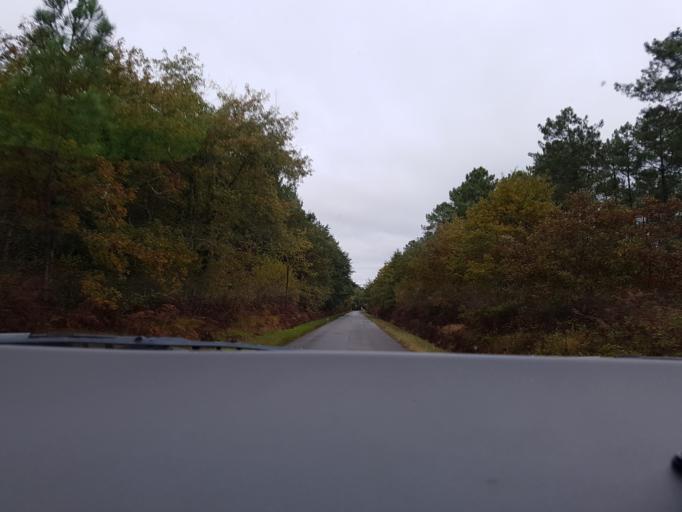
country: FR
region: Aquitaine
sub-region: Departement des Landes
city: Roquefort
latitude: 44.0559
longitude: -0.3471
